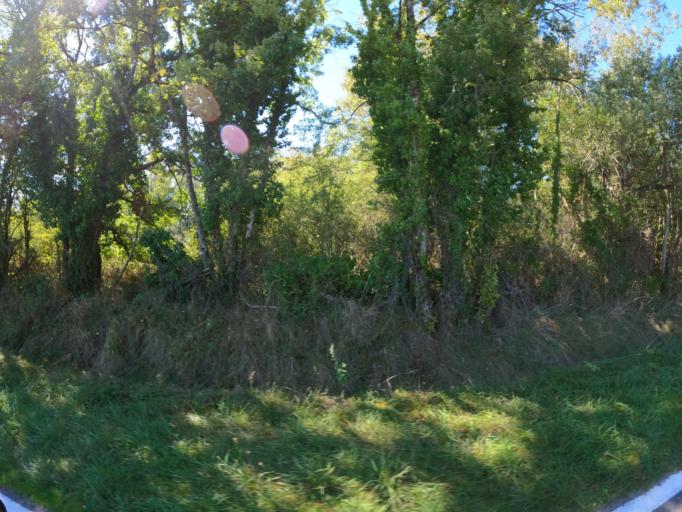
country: FR
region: Poitou-Charentes
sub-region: Departement de la Vienne
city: Lathus-Saint-Remy
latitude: 46.3054
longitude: 0.9860
